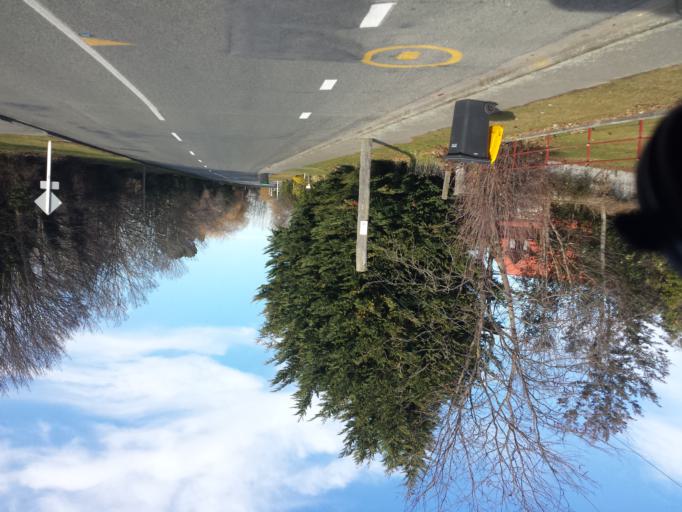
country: NZ
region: Canterbury
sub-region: Timaru District
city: Pleasant Point
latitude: -44.0862
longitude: 171.2459
